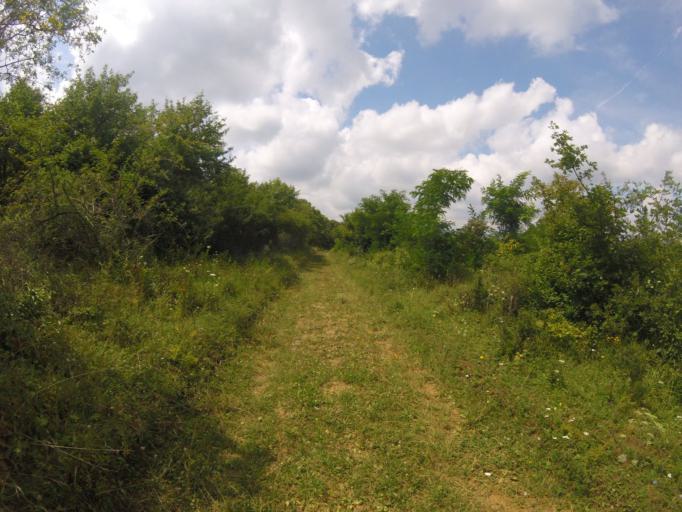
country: SK
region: Nitriansky
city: Sahy
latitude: 48.0244
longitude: 18.9406
